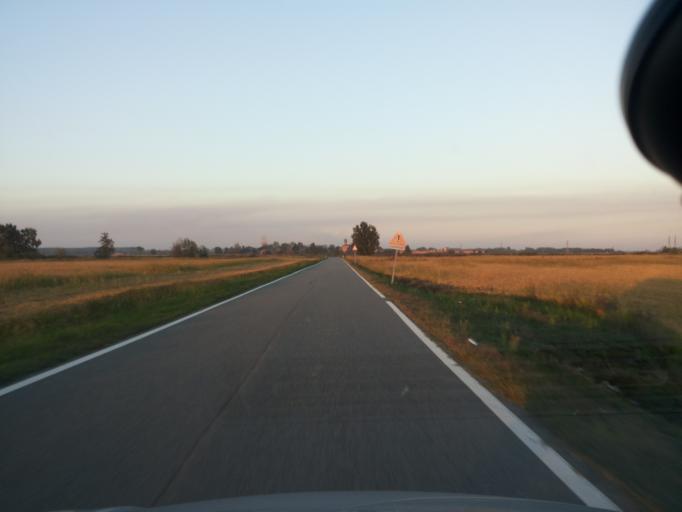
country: IT
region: Piedmont
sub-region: Provincia di Vercelli
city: Carisio
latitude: 45.3886
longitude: 8.2278
